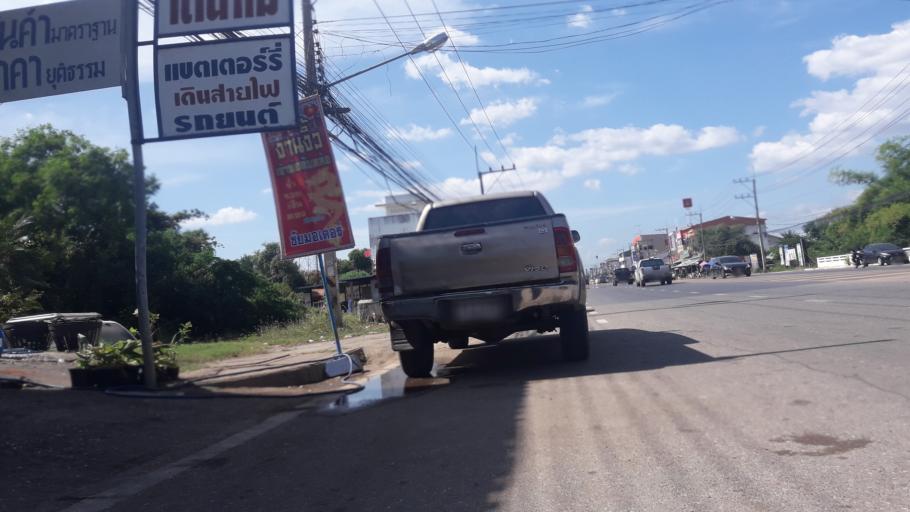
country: TH
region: Phichit
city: Thap Khlo
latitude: 16.1663
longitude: 100.5829
